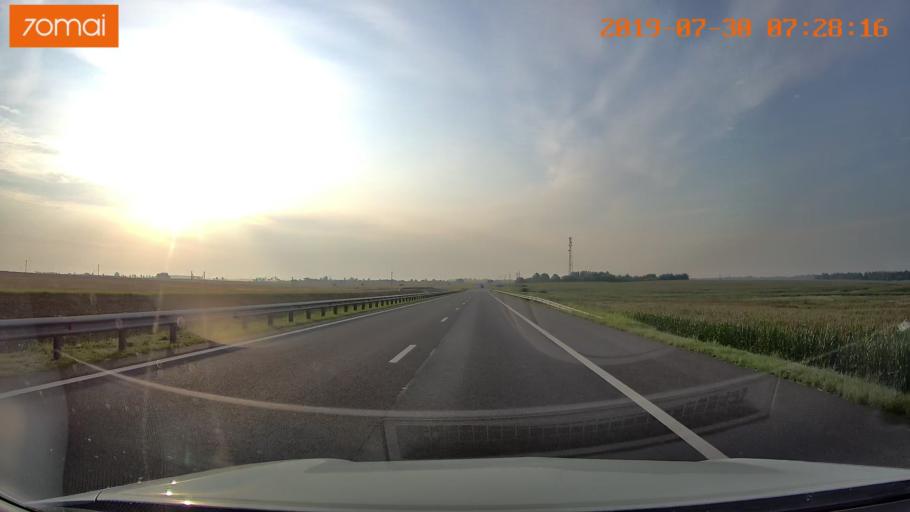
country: RU
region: Kaliningrad
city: Gvardeysk
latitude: 54.6781
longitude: 20.9089
